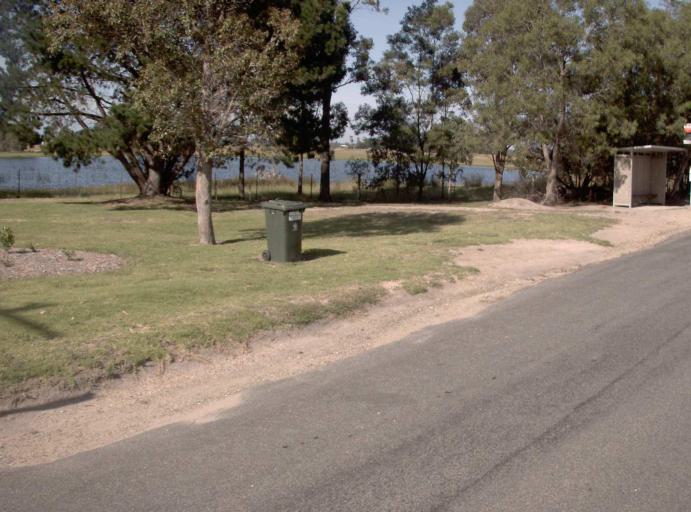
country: AU
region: Victoria
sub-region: East Gippsland
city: Lakes Entrance
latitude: -37.8221
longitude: 147.8571
